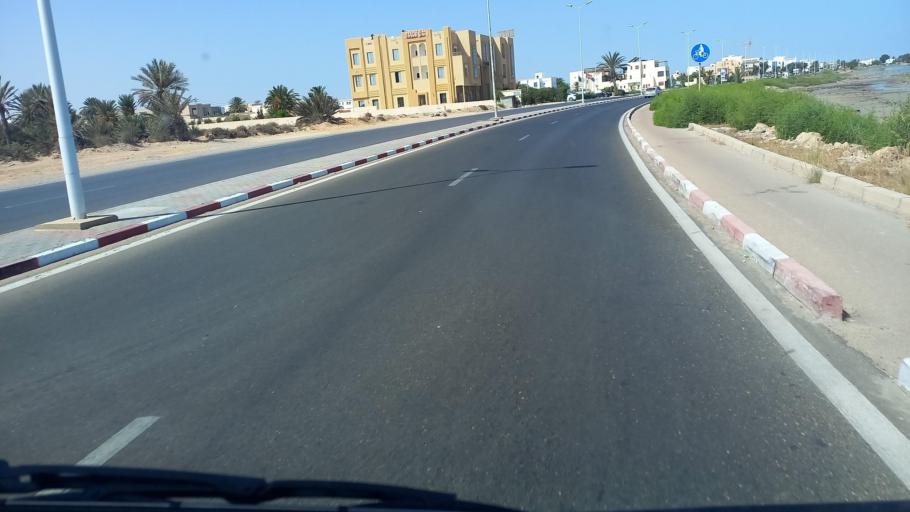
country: TN
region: Madanin
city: Houmt Souk
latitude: 33.8739
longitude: 10.8992
